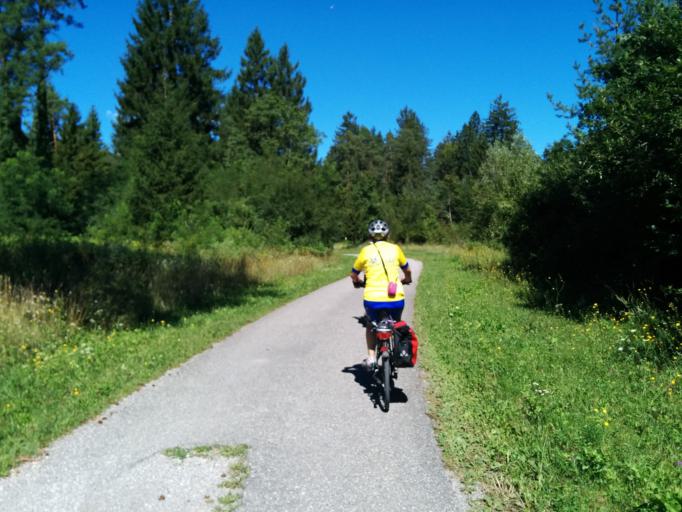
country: IT
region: Friuli Venezia Giulia
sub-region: Provincia di Udine
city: Villa Santina
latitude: 46.4101
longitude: 12.9131
